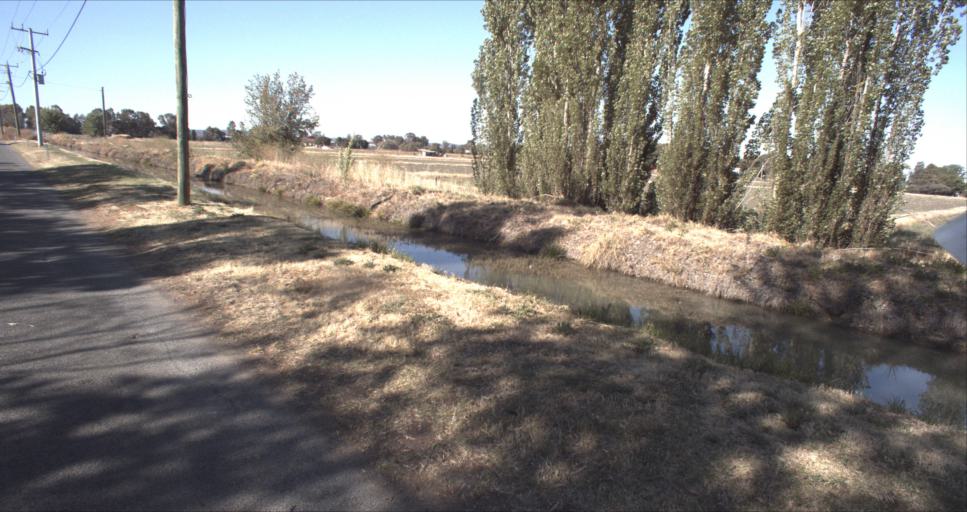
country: AU
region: New South Wales
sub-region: Leeton
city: Leeton
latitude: -34.5419
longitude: 146.4154
